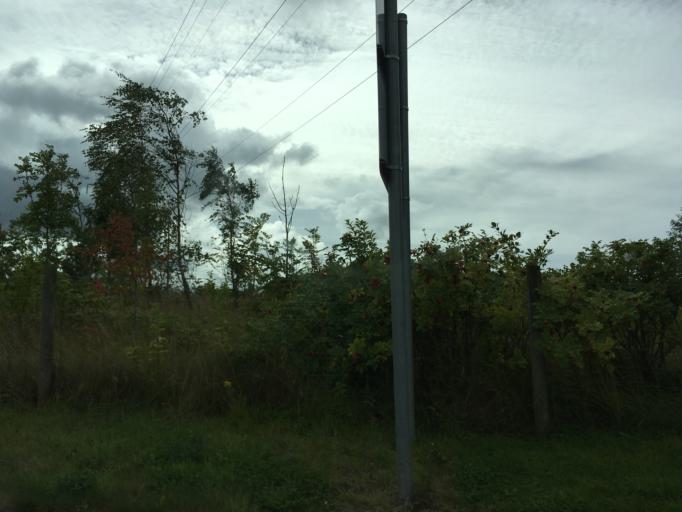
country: IE
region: Leinster
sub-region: Wicklow
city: Ashford
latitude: 53.0434
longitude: -6.0866
